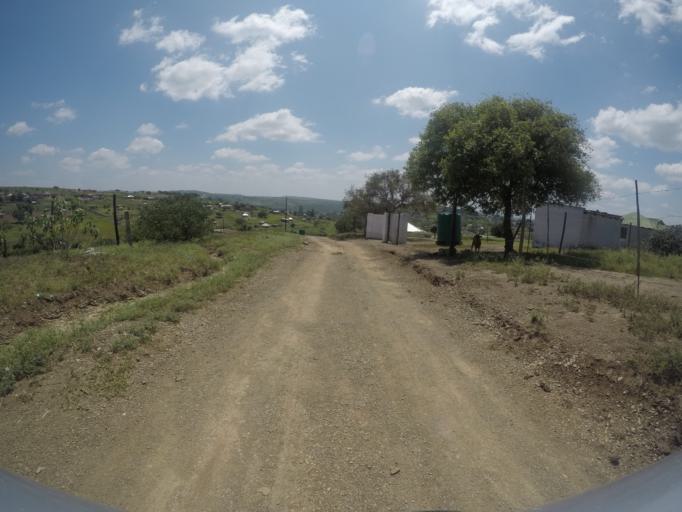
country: ZA
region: KwaZulu-Natal
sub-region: uThungulu District Municipality
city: Empangeni
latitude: -28.6075
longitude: 31.7376
